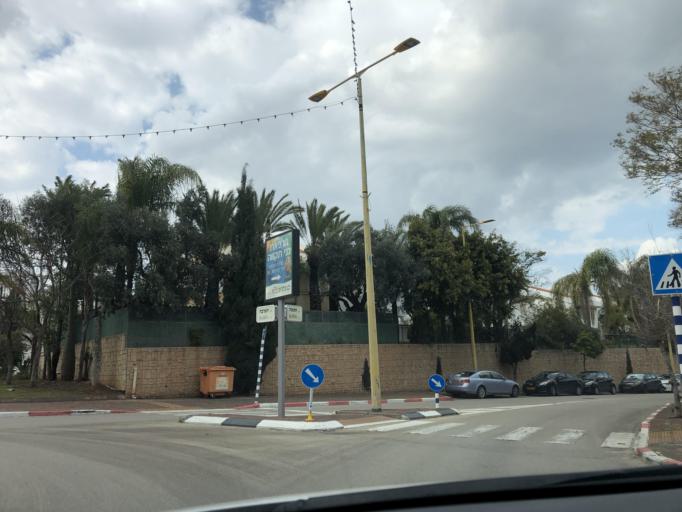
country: IL
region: Central District
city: Ganne Tiqwa
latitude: 32.0619
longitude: 34.8813
